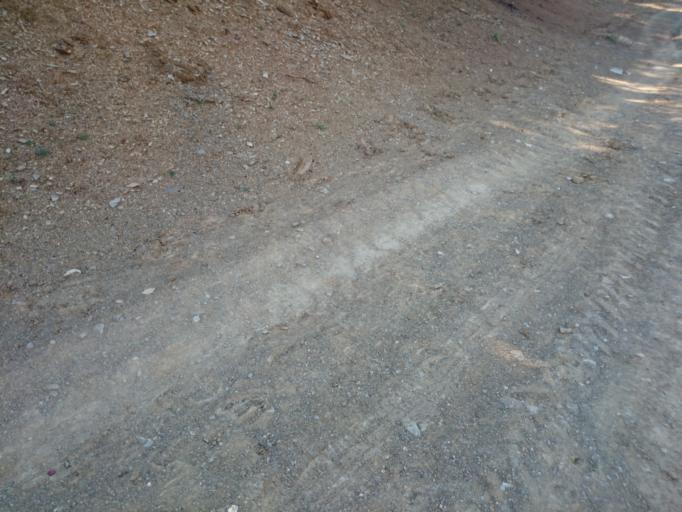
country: AL
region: Diber
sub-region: Rrethi i Bulqizes
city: Zerqan
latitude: 41.4952
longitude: 20.3854
